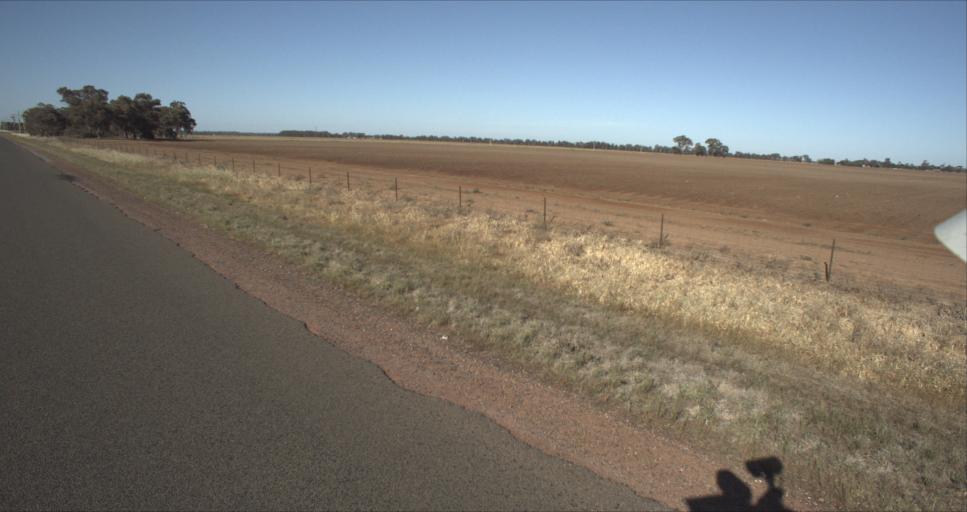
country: AU
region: New South Wales
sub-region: Leeton
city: Leeton
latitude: -34.5745
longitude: 146.2628
